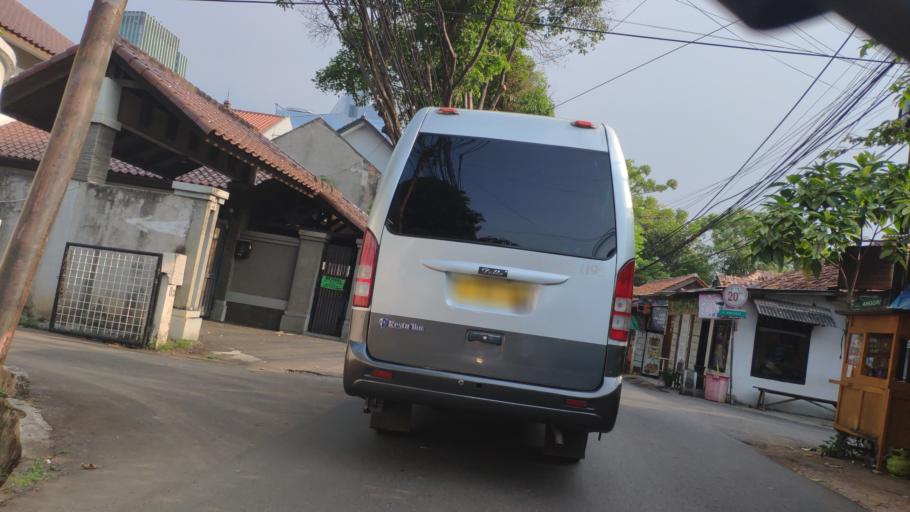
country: ID
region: West Java
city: Pamulang
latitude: -6.2878
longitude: 106.8024
